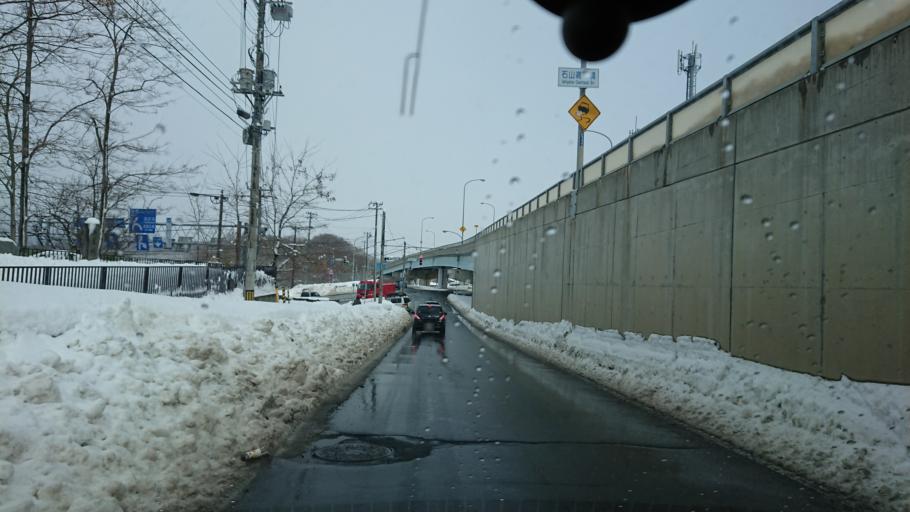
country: JP
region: Hokkaido
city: Sapporo
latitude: 42.9733
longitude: 141.3445
